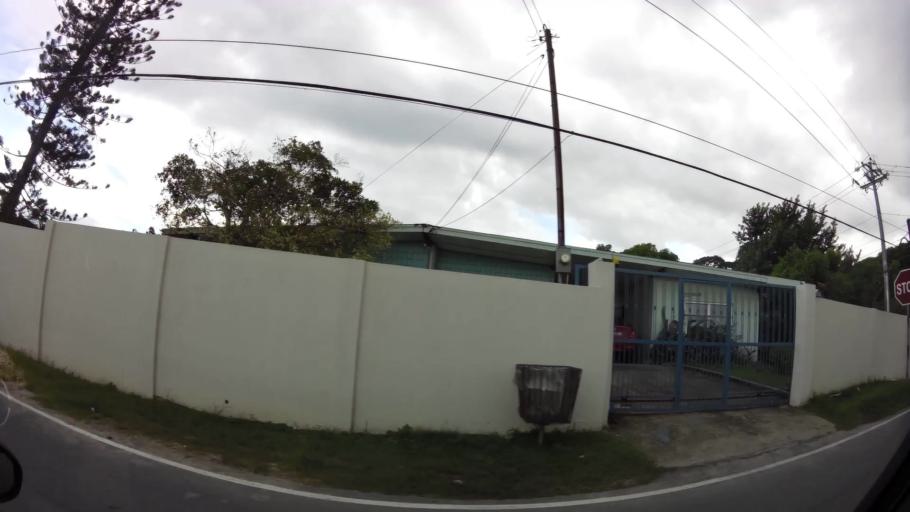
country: TT
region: City of San Fernando
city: Mon Repos
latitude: 10.2489
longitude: -61.4568
